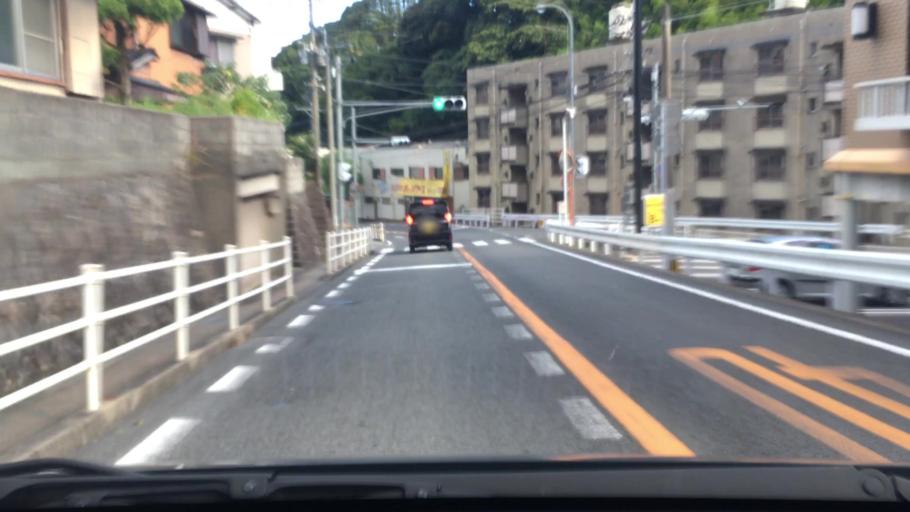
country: JP
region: Nagasaki
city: Togitsu
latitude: 32.8100
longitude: 129.8286
